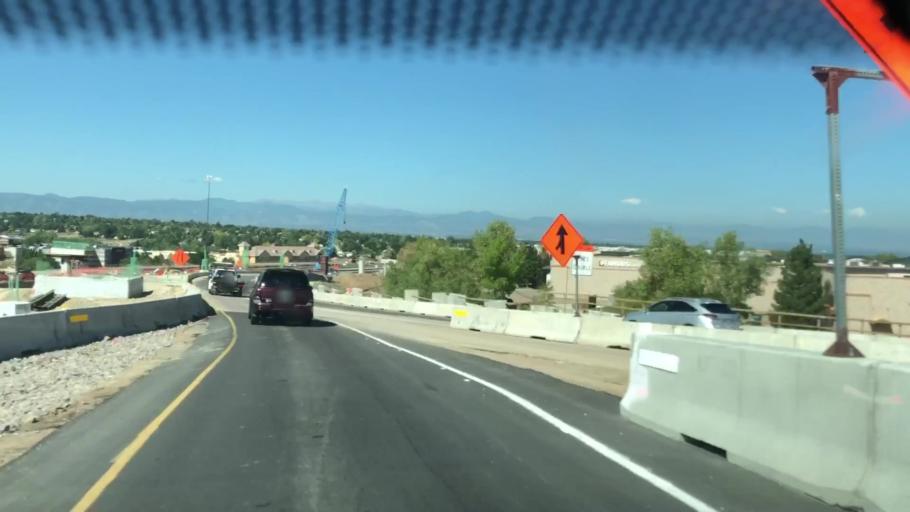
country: US
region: Colorado
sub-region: Adams County
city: Lone Tree
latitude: 39.5565
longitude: -104.8735
